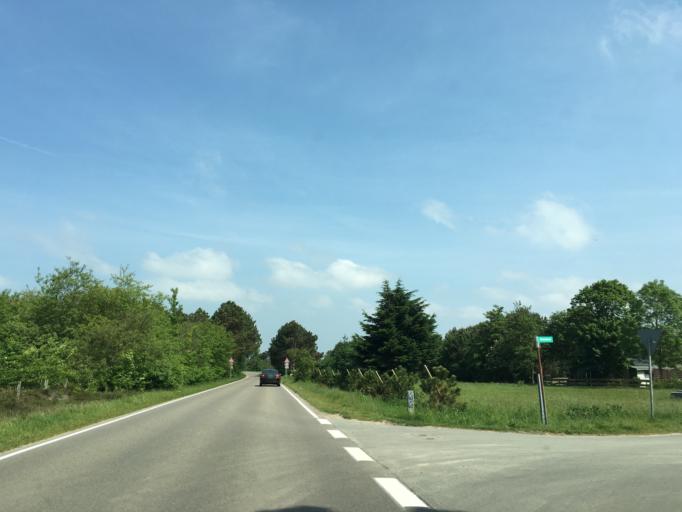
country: DE
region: Schleswig-Holstein
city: Nebel
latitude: 54.6512
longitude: 8.3457
